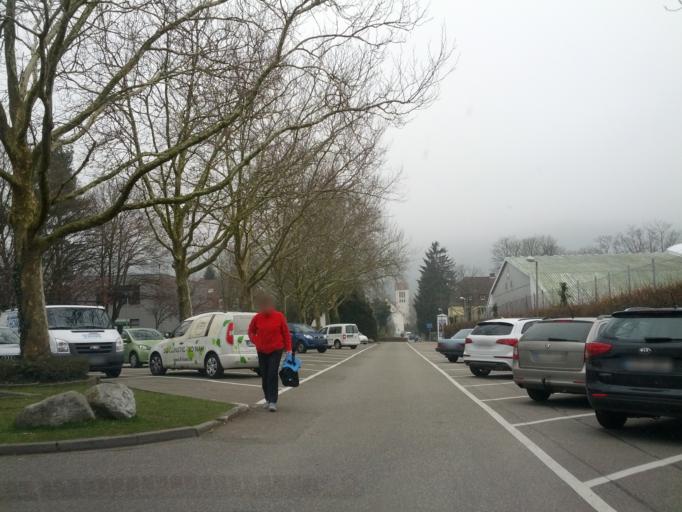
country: DE
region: Baden-Wuerttemberg
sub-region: Freiburg Region
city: Freiburg
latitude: 47.9898
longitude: 7.8846
